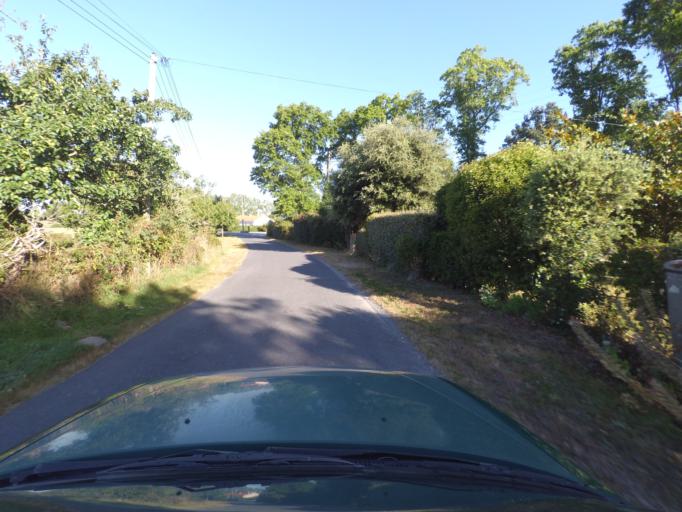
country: FR
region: Pays de la Loire
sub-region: Departement de la Loire-Atlantique
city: Le Bignon
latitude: 47.0916
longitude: -1.4728
